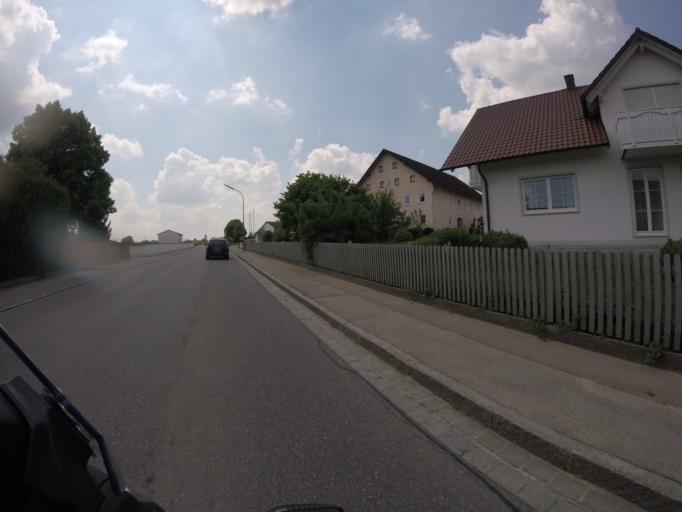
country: DE
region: Bavaria
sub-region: Upper Bavaria
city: Scheyern
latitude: 48.5147
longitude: 11.4628
